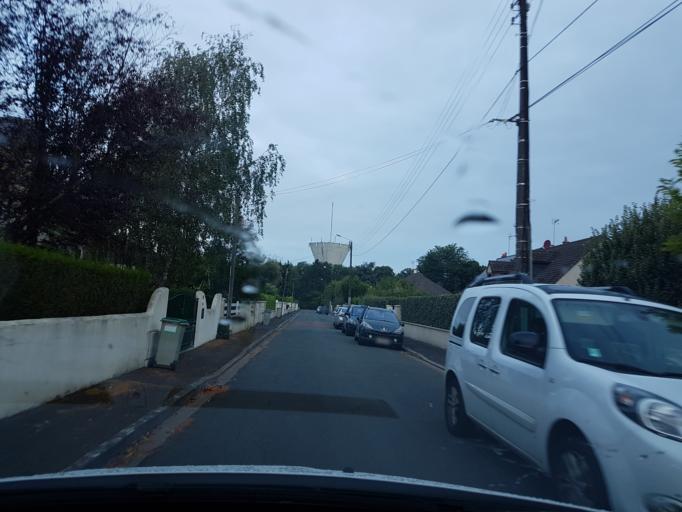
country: FR
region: Centre
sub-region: Departement d'Indre-et-Loire
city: Saint-Avertin
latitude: 47.3680
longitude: 0.7481
